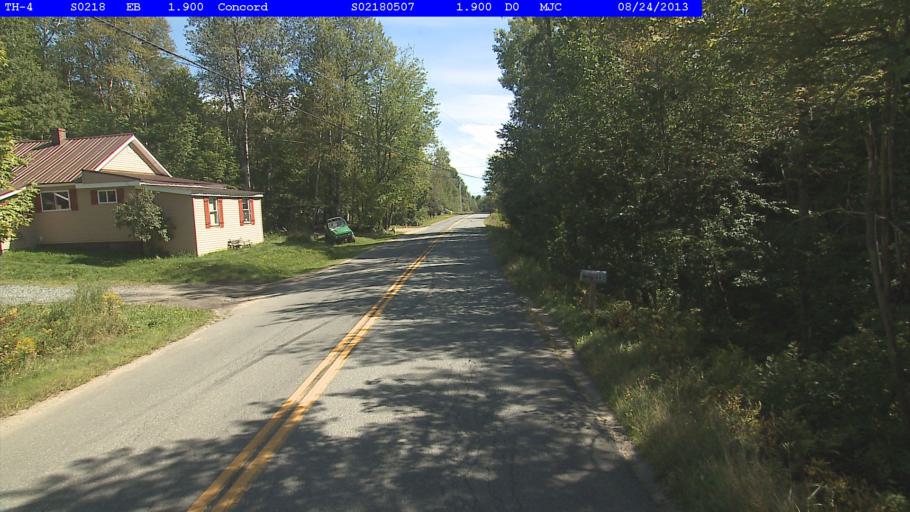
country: US
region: New Hampshire
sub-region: Grafton County
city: Littleton
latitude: 44.4400
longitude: -71.7608
